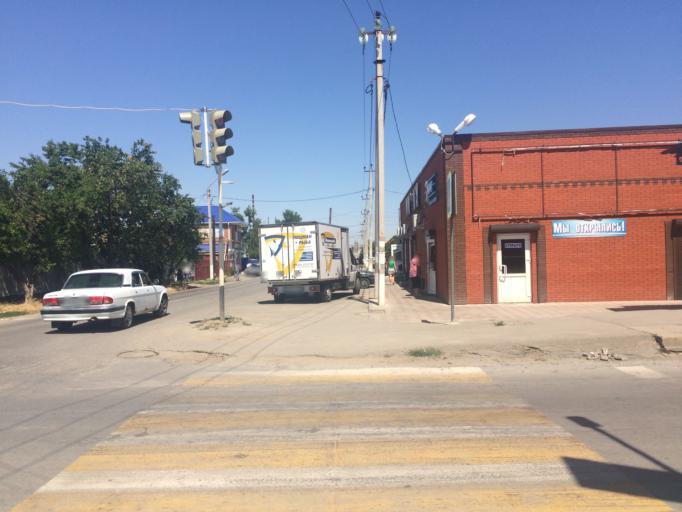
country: RU
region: Rostov
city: Sal'sk
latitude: 46.4689
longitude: 41.5361
